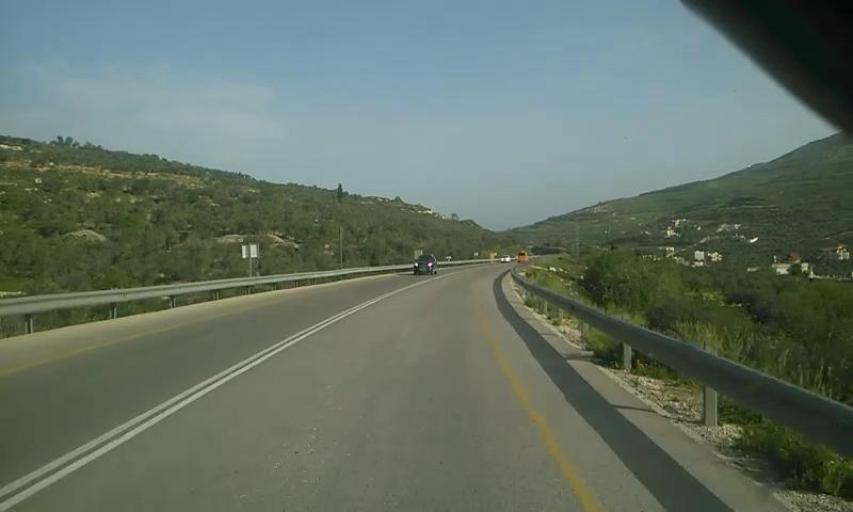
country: PS
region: West Bank
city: Madama
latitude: 32.1878
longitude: 35.2318
